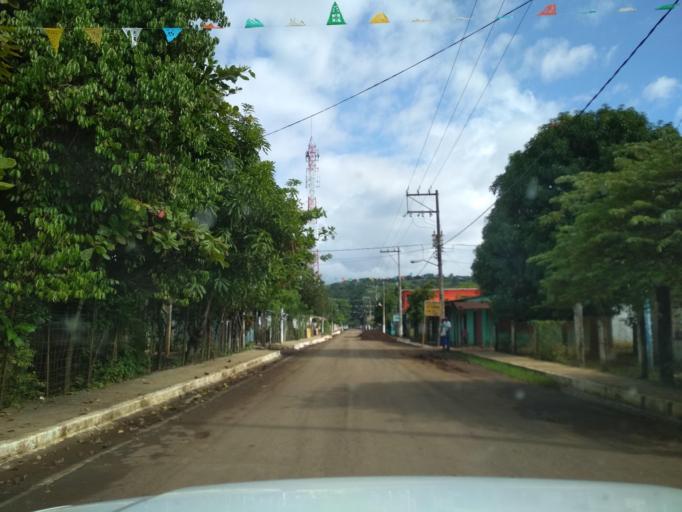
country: MX
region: Veracruz
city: Catemaco
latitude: 18.3747
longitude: -95.1223
